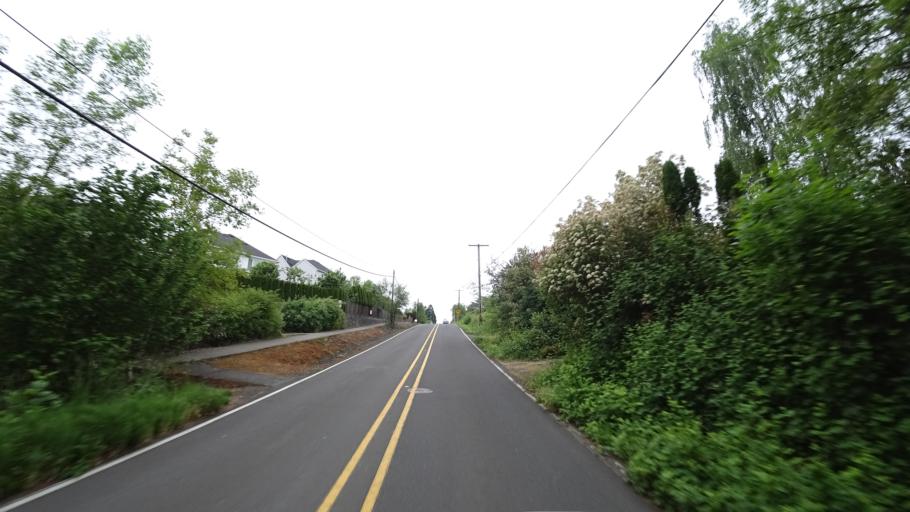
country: US
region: Oregon
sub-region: Washington County
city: Bethany
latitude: 45.5517
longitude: -122.8574
